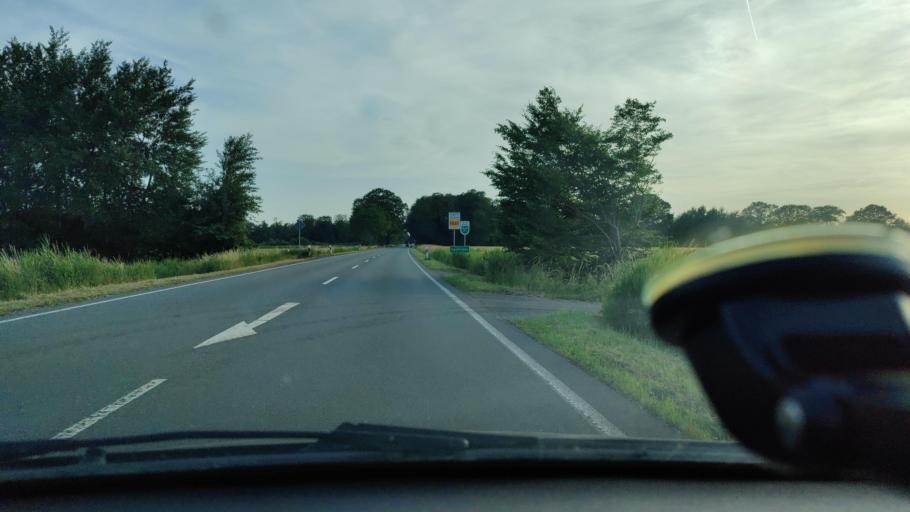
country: DE
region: North Rhine-Westphalia
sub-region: Regierungsbezirk Munster
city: Legden
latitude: 51.9755
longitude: 7.0905
